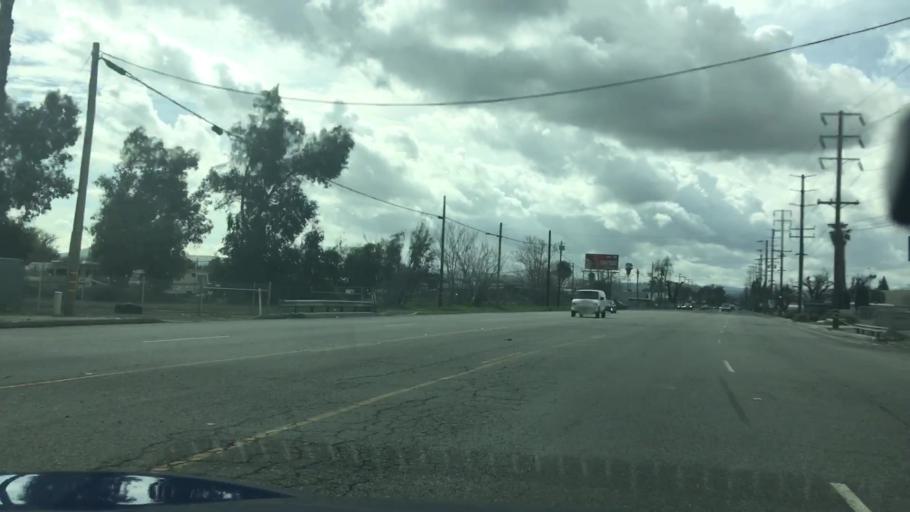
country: US
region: California
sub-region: Riverside County
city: Highgrove
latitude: 34.0208
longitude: -117.3625
